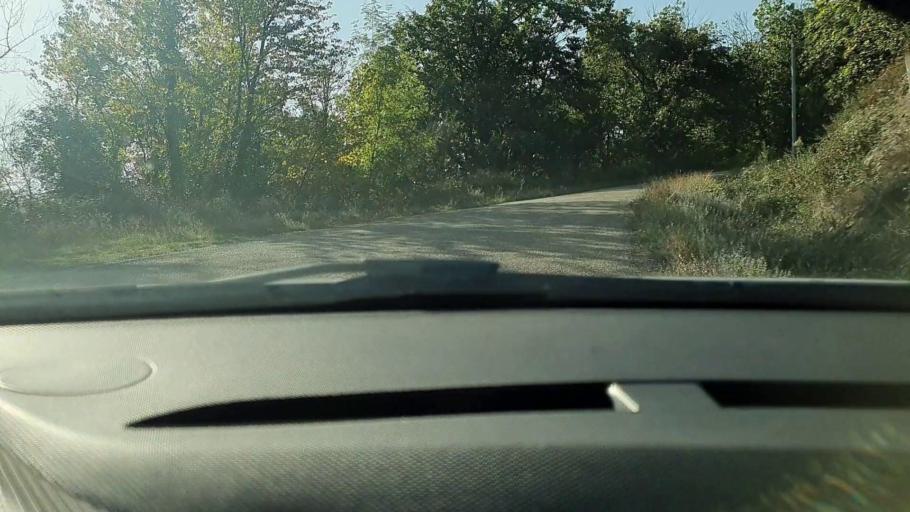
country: FR
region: Languedoc-Roussillon
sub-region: Departement du Gard
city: Besseges
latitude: 44.3163
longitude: 4.0504
